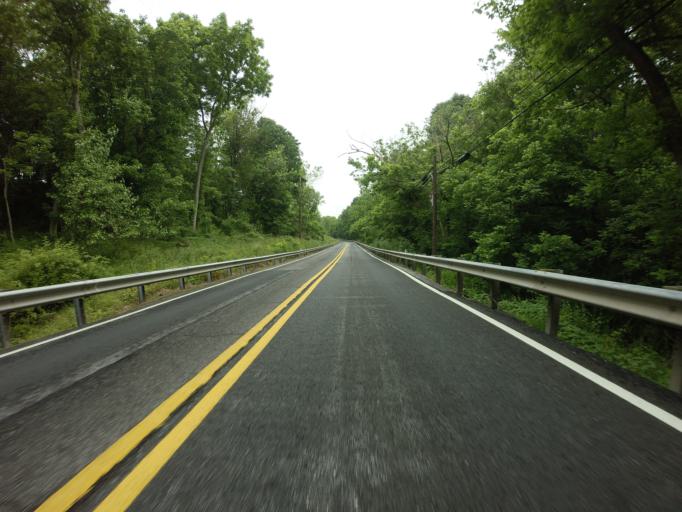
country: US
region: Maryland
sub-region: Frederick County
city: Jefferson
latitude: 39.3299
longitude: -77.5557
